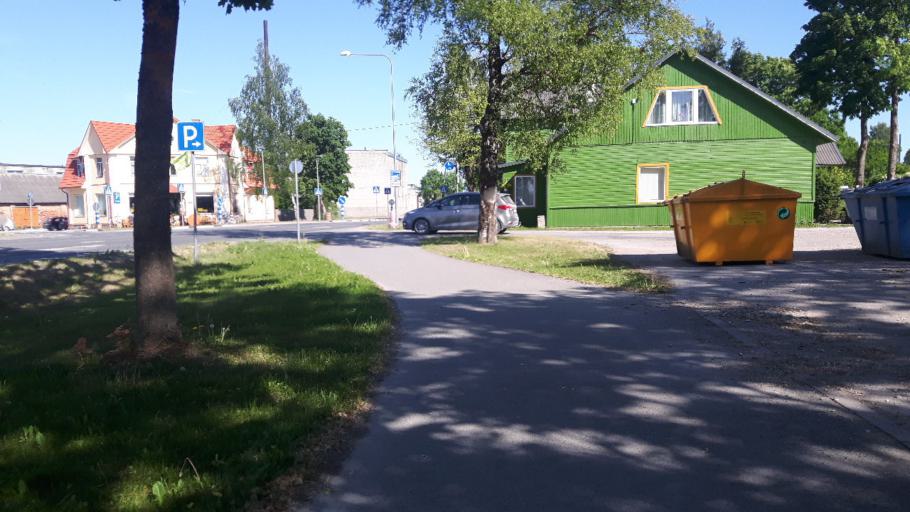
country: EE
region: Raplamaa
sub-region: Rapla vald
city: Rapla
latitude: 58.9923
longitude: 24.8288
